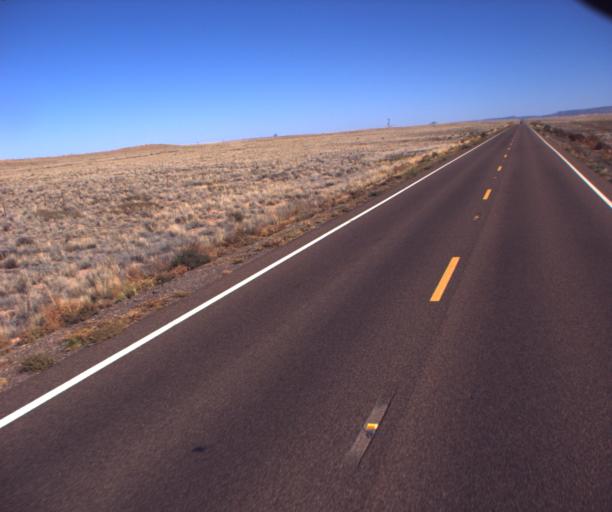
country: US
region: Arizona
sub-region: Navajo County
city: Winslow
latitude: 35.1250
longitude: -110.5035
